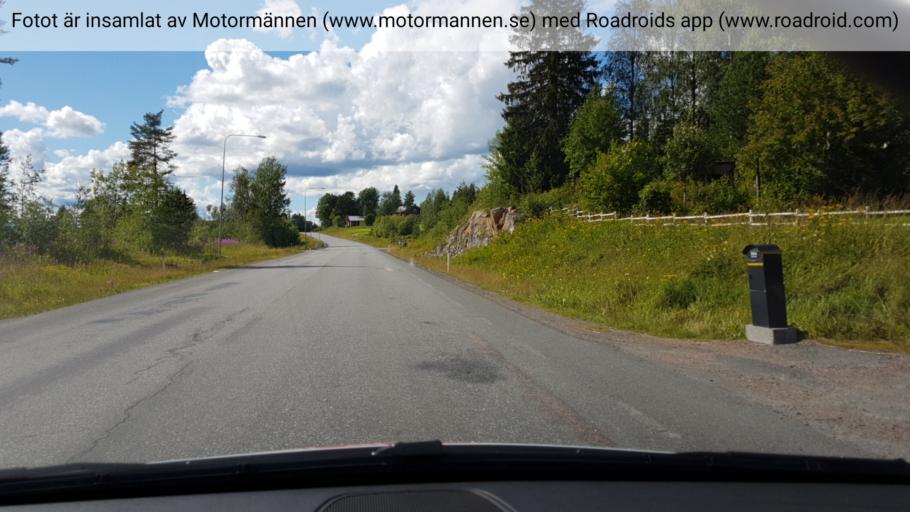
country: SE
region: Jaemtland
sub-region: Ragunda Kommun
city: Hammarstrand
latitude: 63.0357
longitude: 16.5680
